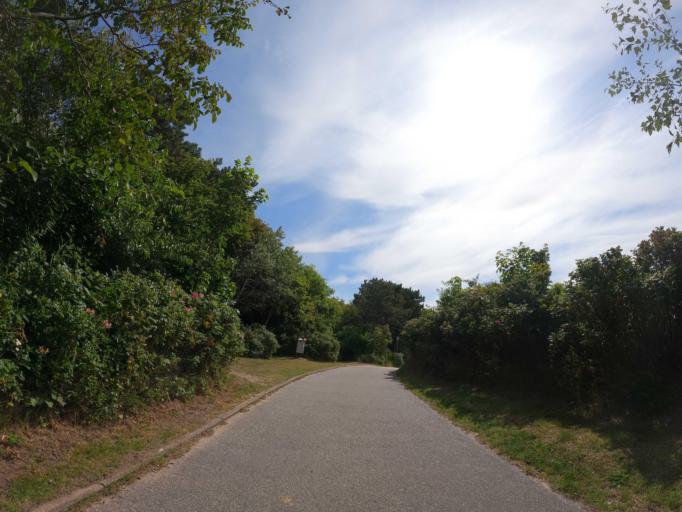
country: DE
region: Schleswig-Holstein
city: Westerland
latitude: 54.9260
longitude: 8.3163
